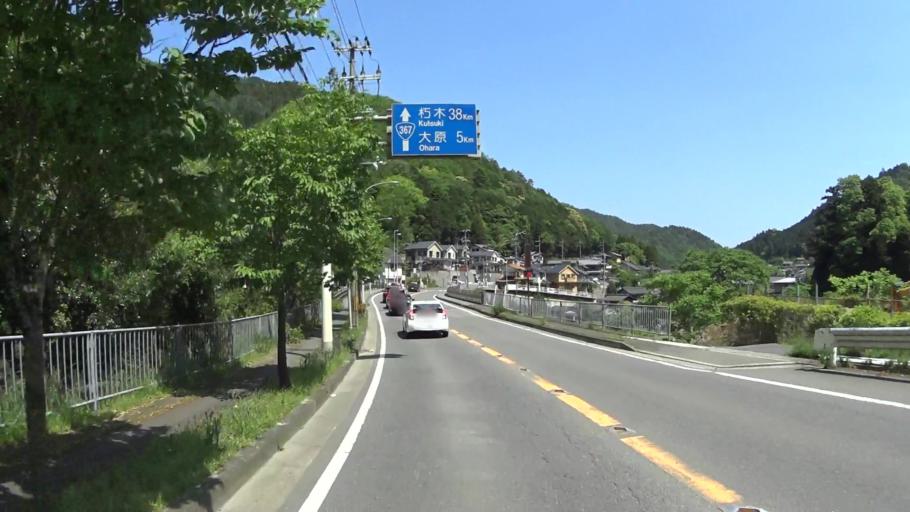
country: JP
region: Kyoto
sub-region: Kyoto-shi
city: Kamigyo-ku
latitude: 35.0772
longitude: 135.8179
